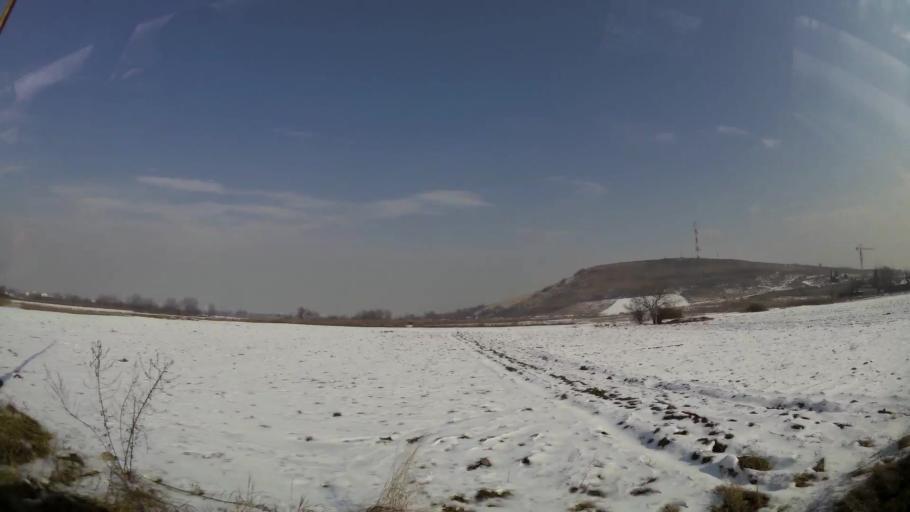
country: MK
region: Suto Orizari
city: Suto Orizare
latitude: 42.0181
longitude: 21.3884
